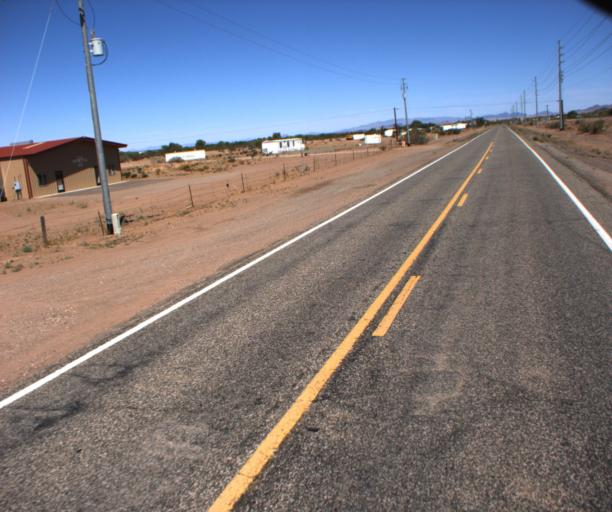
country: US
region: Arizona
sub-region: La Paz County
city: Cienega Springs
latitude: 33.9388
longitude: -114.0105
